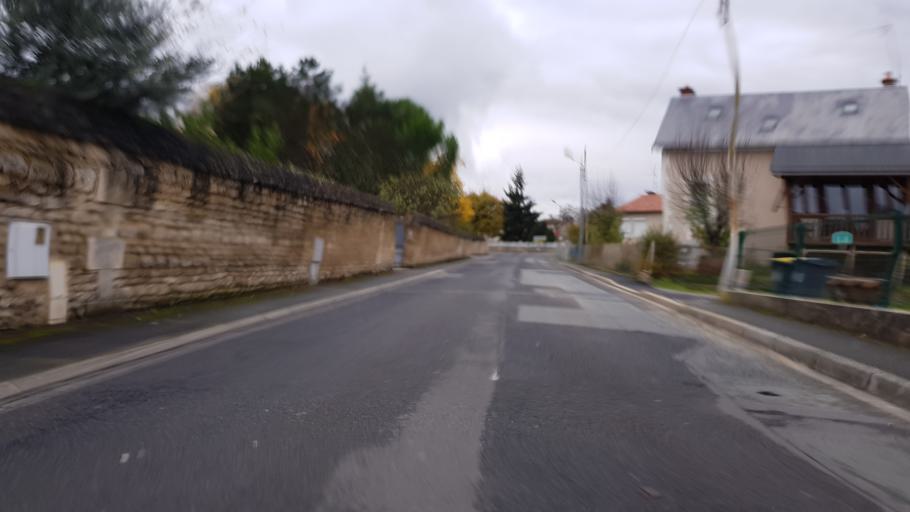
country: FR
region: Poitou-Charentes
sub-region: Departement de la Vienne
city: Chasseneuil-du-Poitou
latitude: 46.6531
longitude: 0.3782
